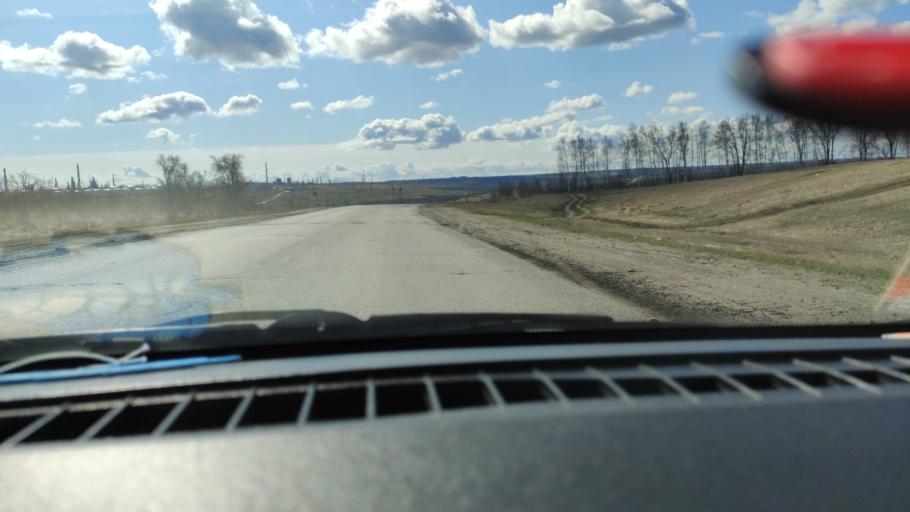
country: RU
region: Samara
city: Varlamovo
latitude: 53.1033
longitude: 48.3573
